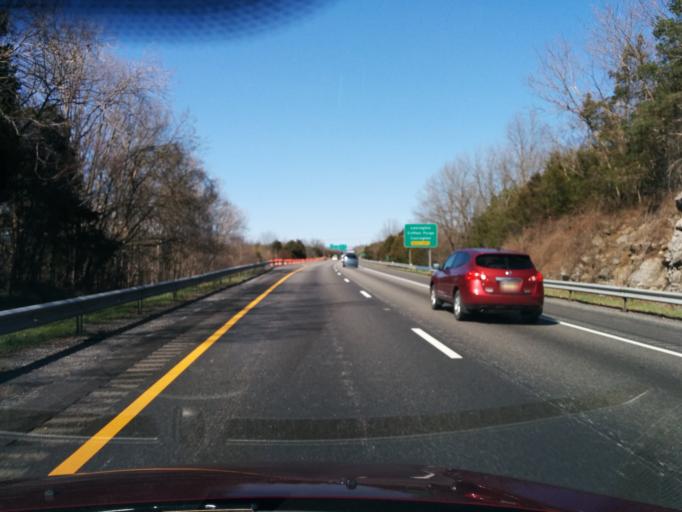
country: US
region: Virginia
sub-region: Rockbridge County
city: East Lexington
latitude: 37.7863
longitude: -79.3995
